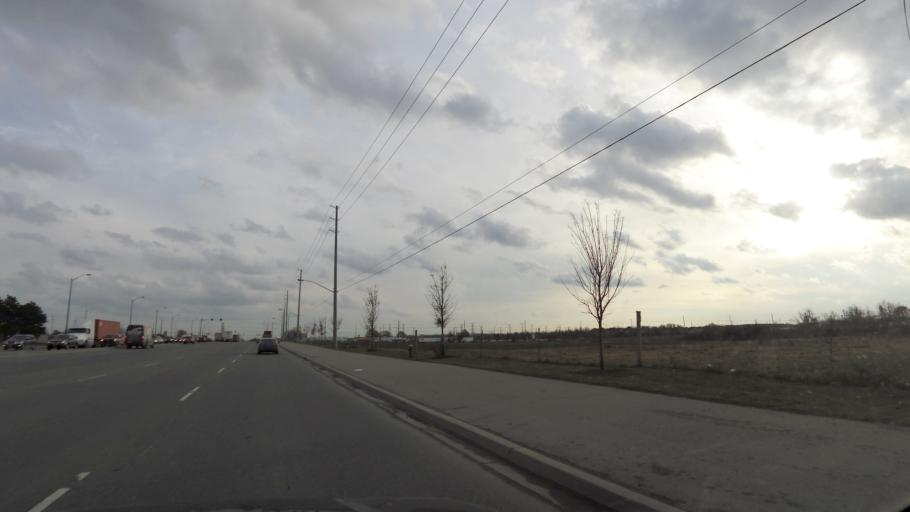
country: CA
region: Ontario
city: Etobicoke
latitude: 43.7703
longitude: -79.6504
